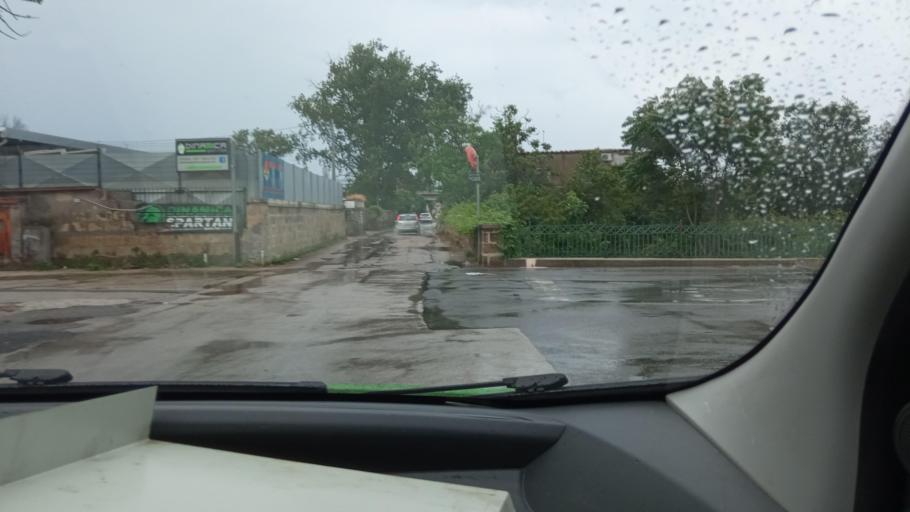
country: IT
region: Campania
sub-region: Provincia di Napoli
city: Pozzuoli
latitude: 40.8401
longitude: 14.1176
